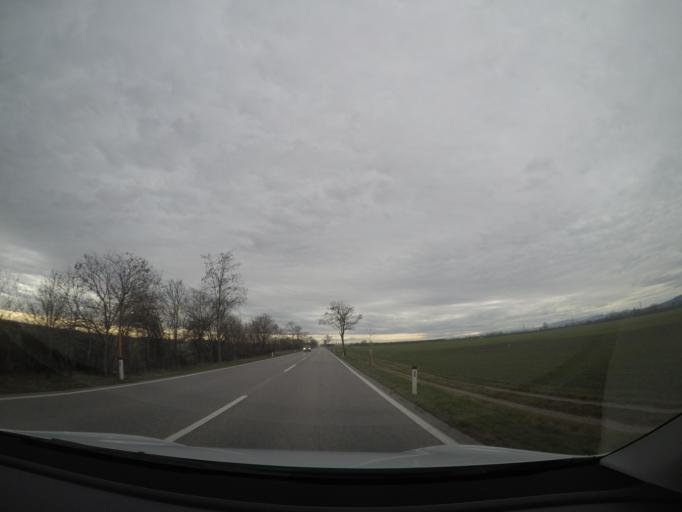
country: AT
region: Lower Austria
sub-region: Politischer Bezirk Modling
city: Munchendorf
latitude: 48.0548
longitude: 16.3822
